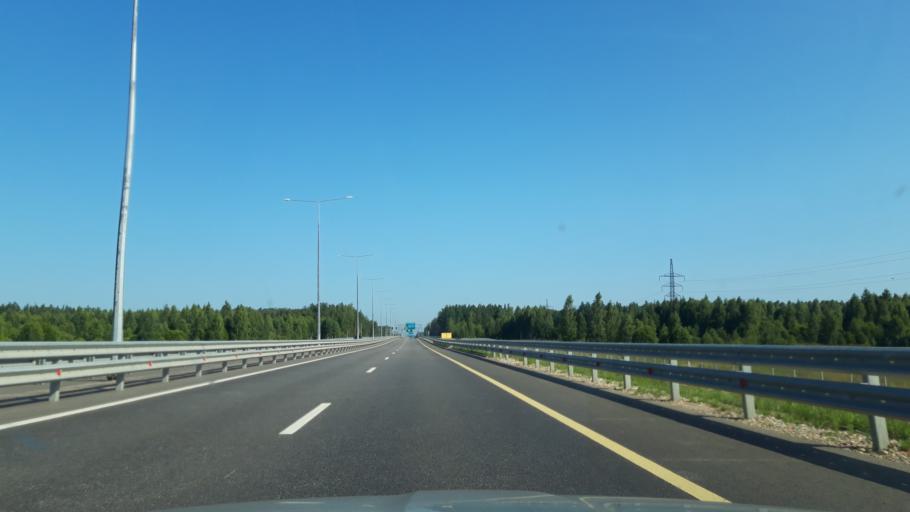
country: RU
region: Tverskaya
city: Zavidovo
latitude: 56.5544
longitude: 36.4867
